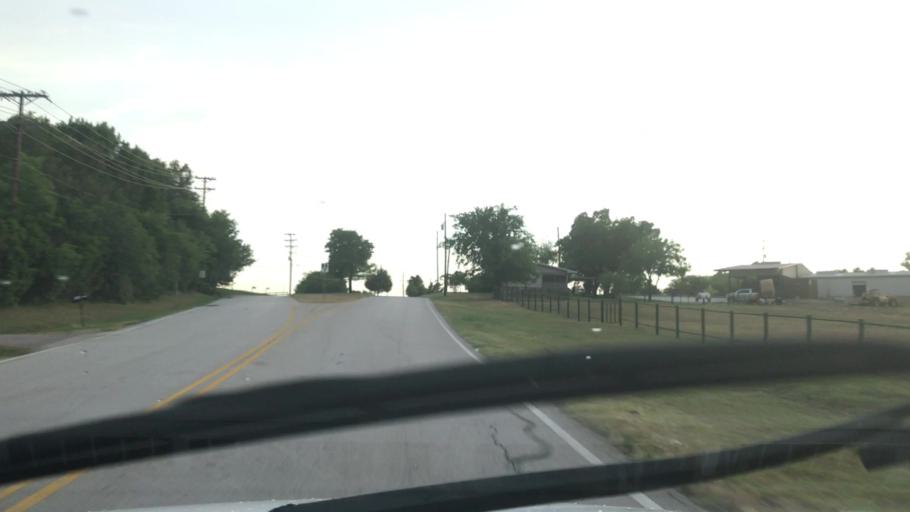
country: US
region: Texas
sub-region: Dallas County
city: Balch Springs
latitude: 32.7096
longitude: -96.5561
